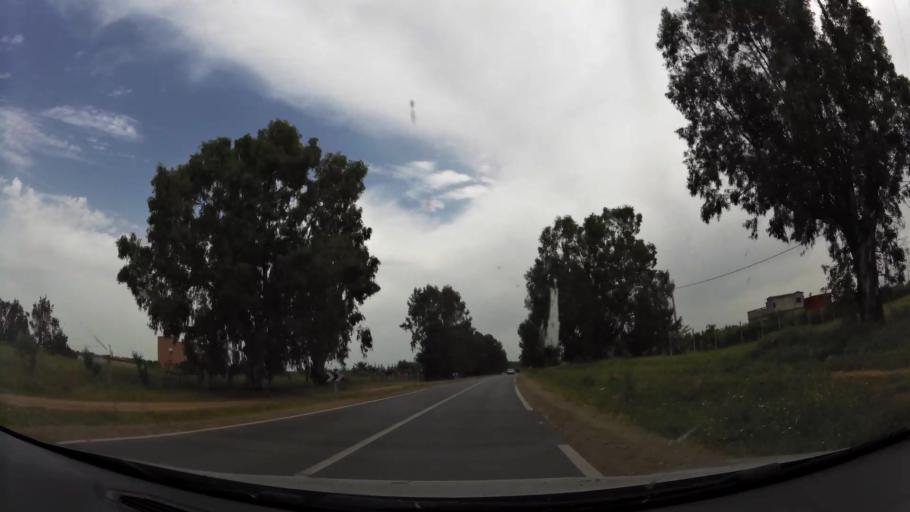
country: MA
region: Rabat-Sale-Zemmour-Zaer
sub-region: Khemisset
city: Tiflet
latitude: 33.8523
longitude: -6.2683
